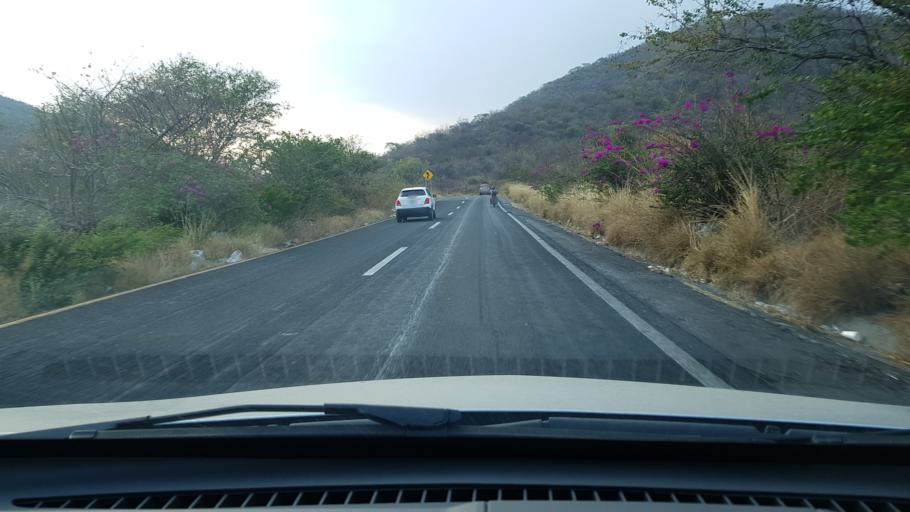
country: MX
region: Morelos
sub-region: Jiutepec
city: Independencia
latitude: 18.8572
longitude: -99.1149
